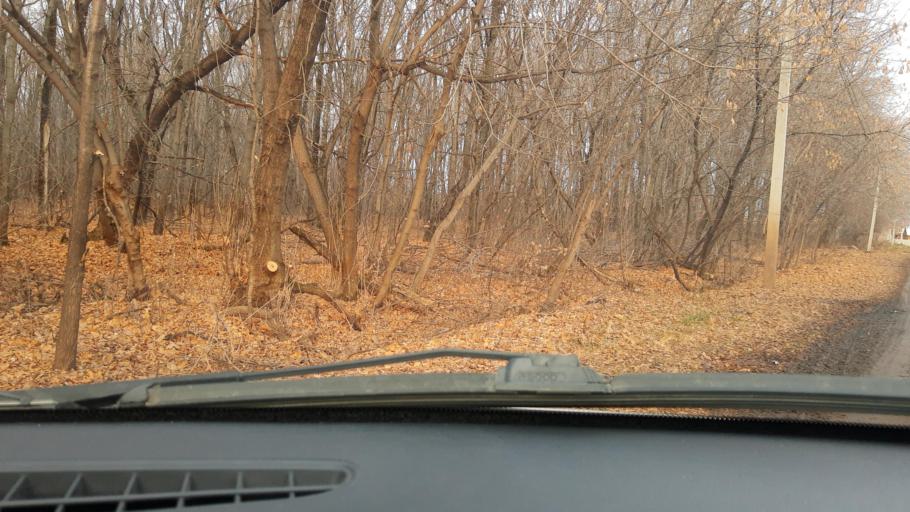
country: RU
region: Bashkortostan
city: Avdon
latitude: 54.6863
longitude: 55.7930
